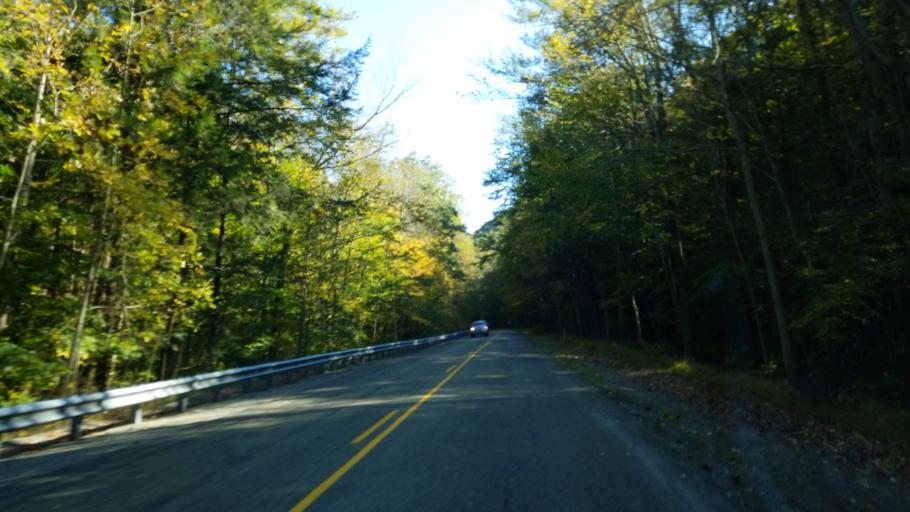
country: US
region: Pennsylvania
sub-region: Clearfield County
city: Shiloh
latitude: 41.2567
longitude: -78.3867
